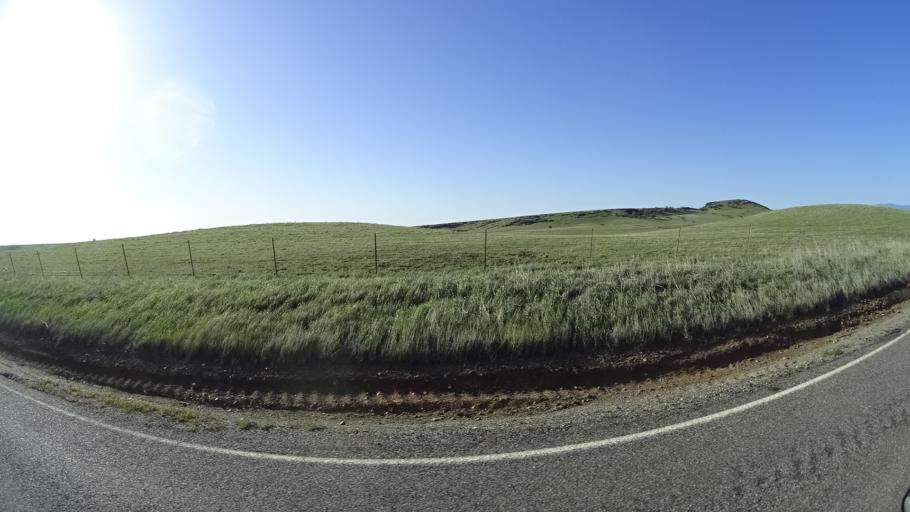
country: US
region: California
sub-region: Glenn County
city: Orland
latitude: 39.8314
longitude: -122.3456
